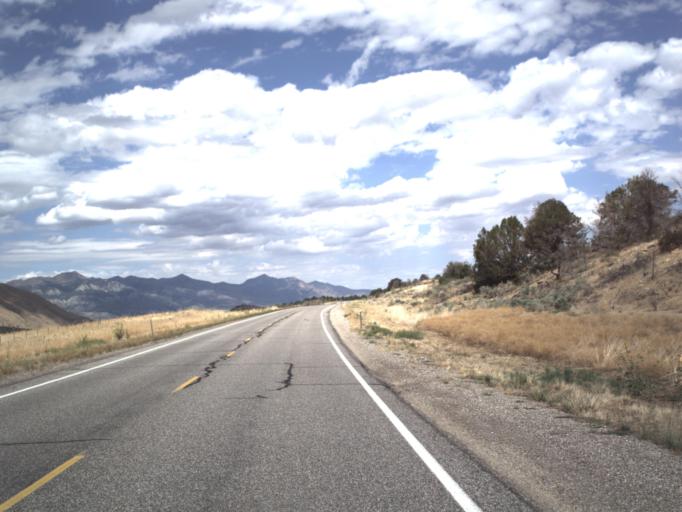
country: US
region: Utah
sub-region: Sanpete County
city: Gunnison
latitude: 39.1572
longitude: -112.0695
